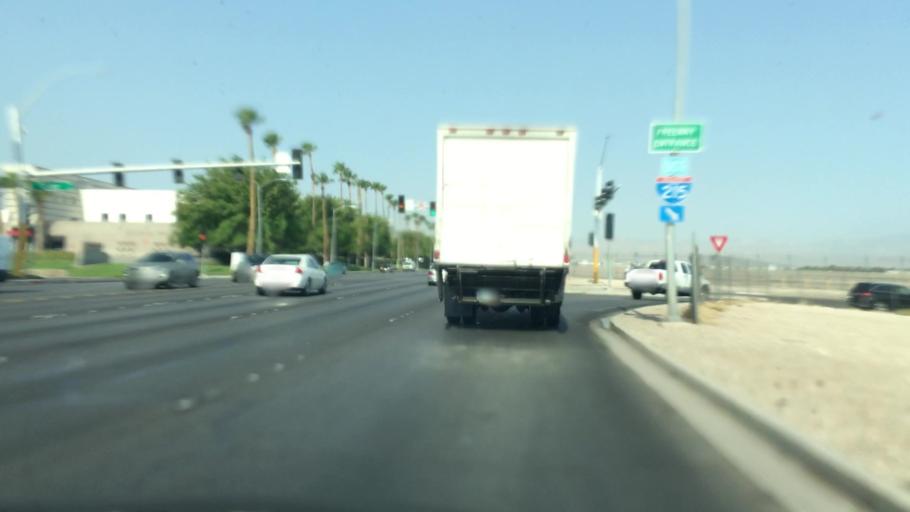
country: US
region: Nevada
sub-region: Clark County
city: Paradise
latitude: 36.0716
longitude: -115.1477
